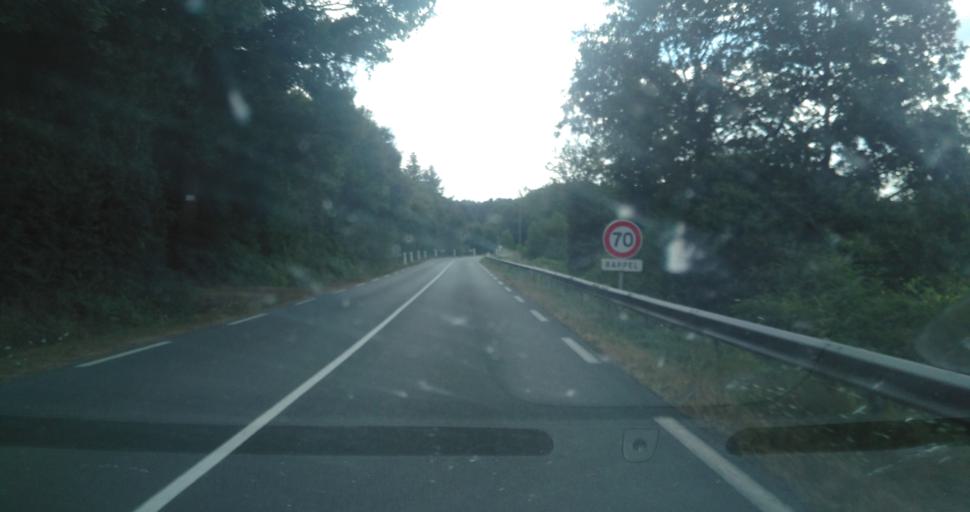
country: FR
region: Pays de la Loire
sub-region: Departement de la Vendee
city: Bournezeau
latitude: 46.5910
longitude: -1.1185
